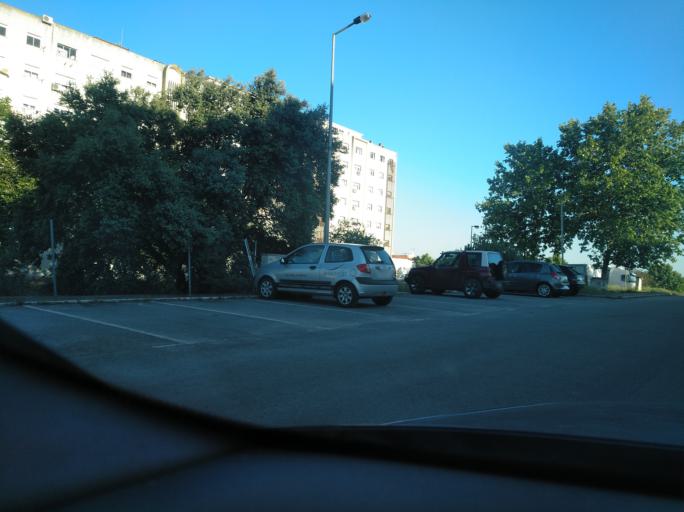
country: PT
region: Portalegre
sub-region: Elvas
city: Elvas
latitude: 38.8772
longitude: -7.1846
